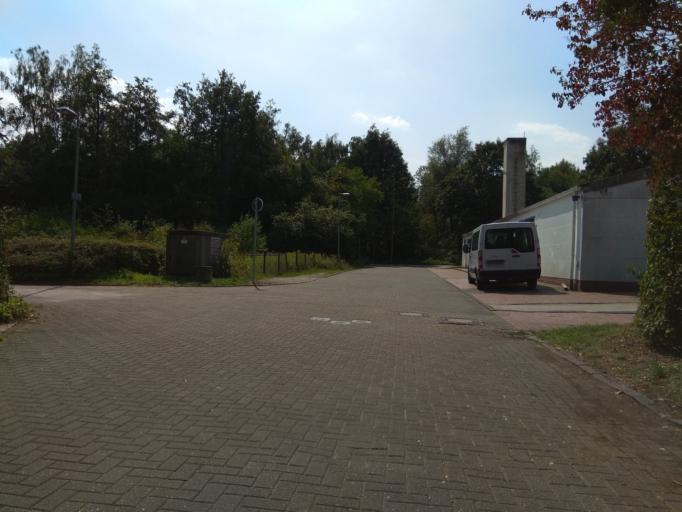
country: DE
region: North Rhine-Westphalia
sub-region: Regierungsbezirk Munster
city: Klein Reken
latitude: 51.7236
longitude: 7.0319
